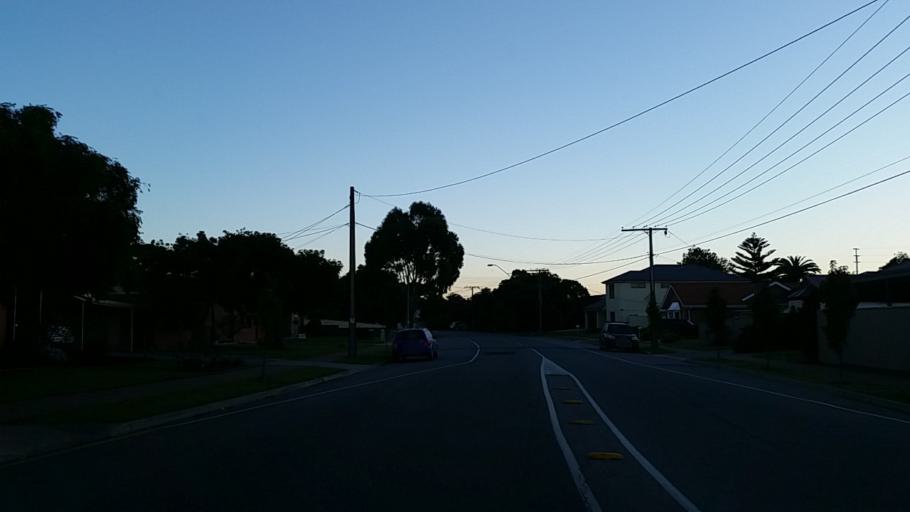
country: AU
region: South Australia
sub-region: Charles Sturt
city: Henley Beach
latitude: -34.9224
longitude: 138.5047
